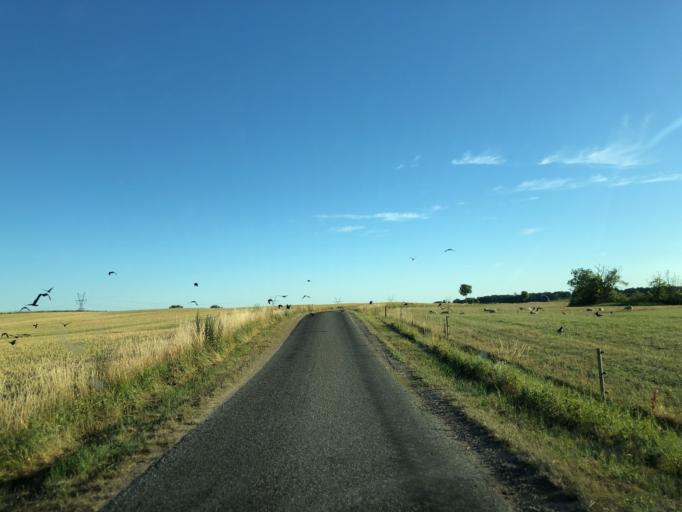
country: DK
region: Central Jutland
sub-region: Horsens Kommune
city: Horsens
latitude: 55.9204
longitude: 9.8887
